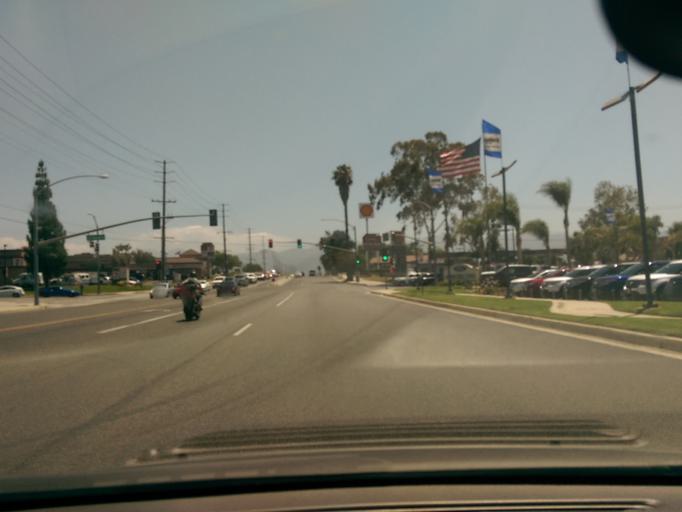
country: US
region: California
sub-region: Riverside County
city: Norco
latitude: 33.9103
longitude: -117.5611
